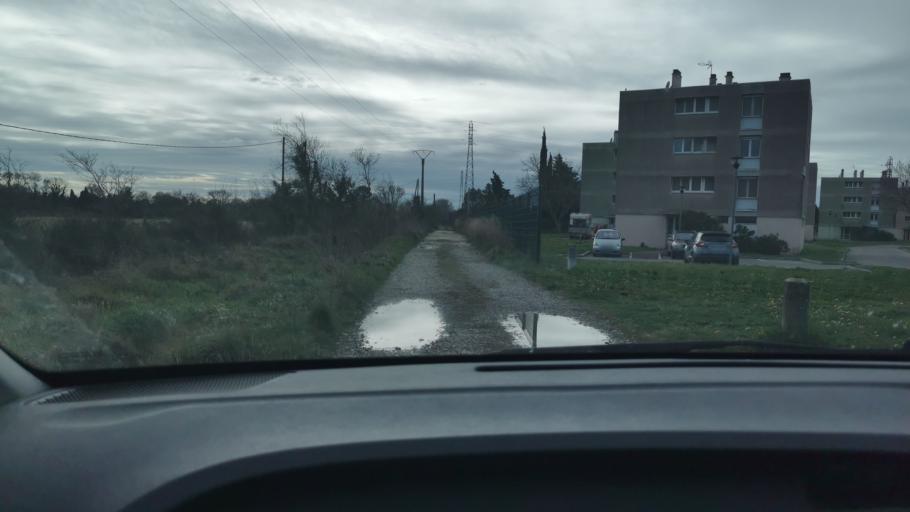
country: FR
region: Provence-Alpes-Cote d'Azur
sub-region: Departement des Bouches-du-Rhone
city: Miramas
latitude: 43.5783
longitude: 4.9906
